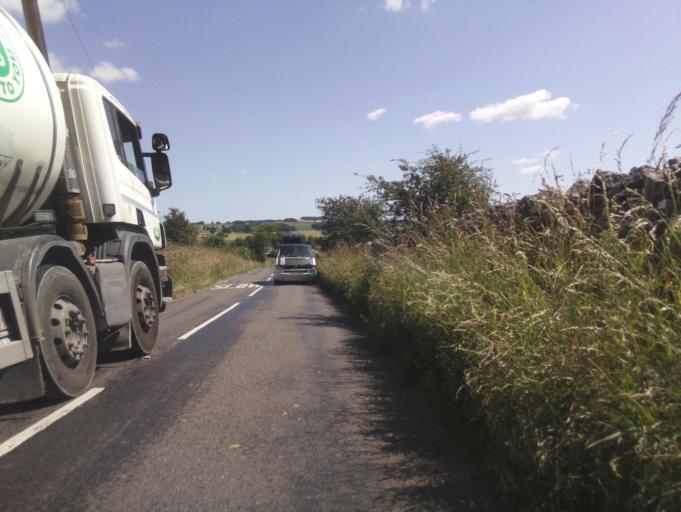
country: GB
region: England
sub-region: Derbyshire
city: Tideswell
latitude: 53.1954
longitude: -1.7840
